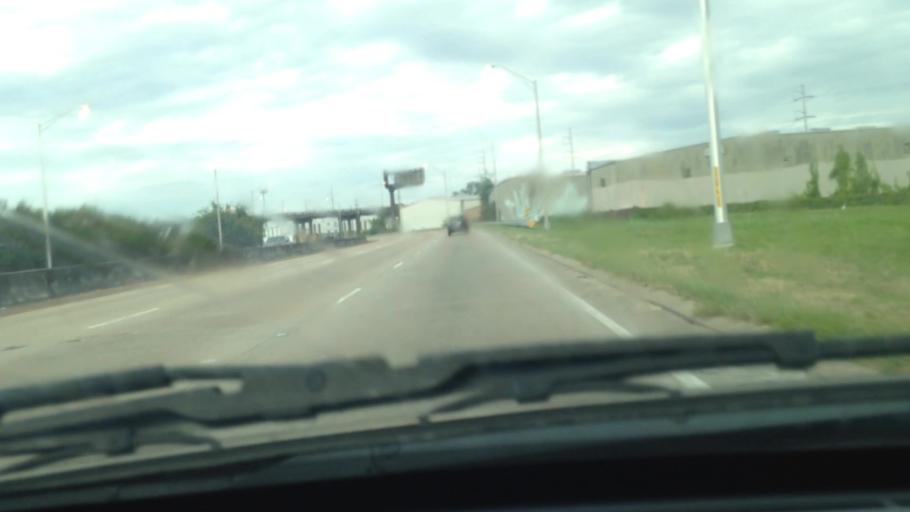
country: US
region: Louisiana
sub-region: Jefferson Parish
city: Jefferson
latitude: 29.9710
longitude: -90.1534
